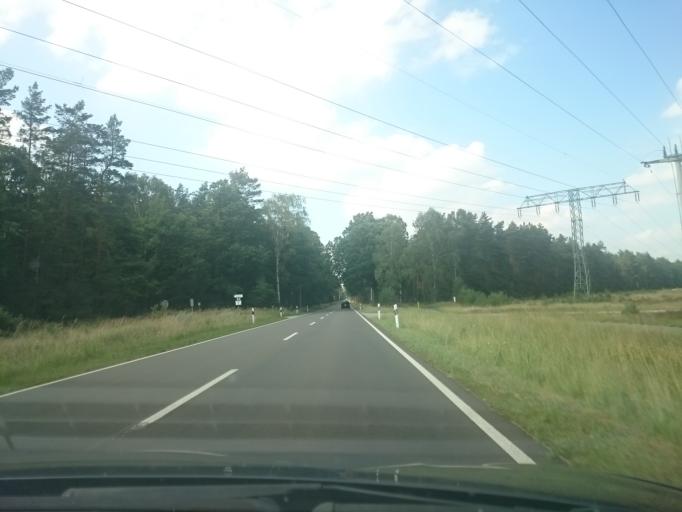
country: DE
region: Mecklenburg-Vorpommern
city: Viereck
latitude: 53.5981
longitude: 14.0548
